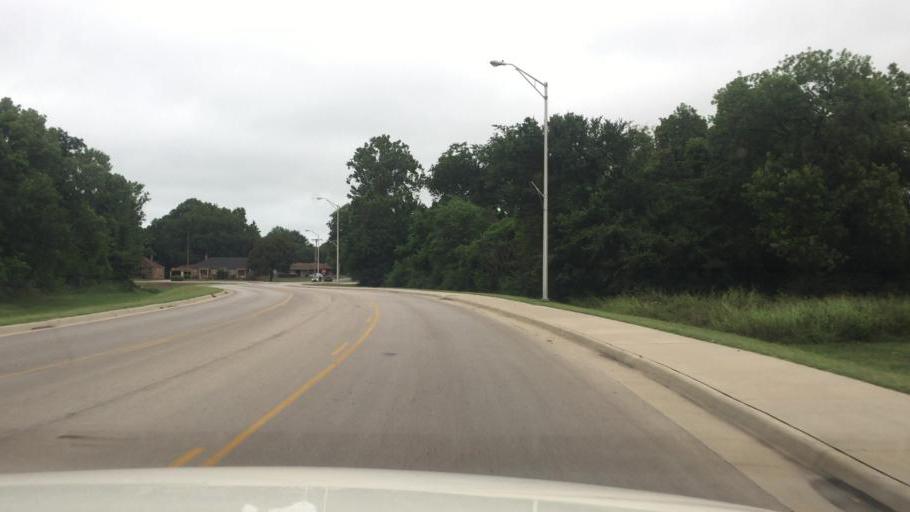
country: US
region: Kansas
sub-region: Montgomery County
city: Coffeyville
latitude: 37.0345
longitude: -95.6467
